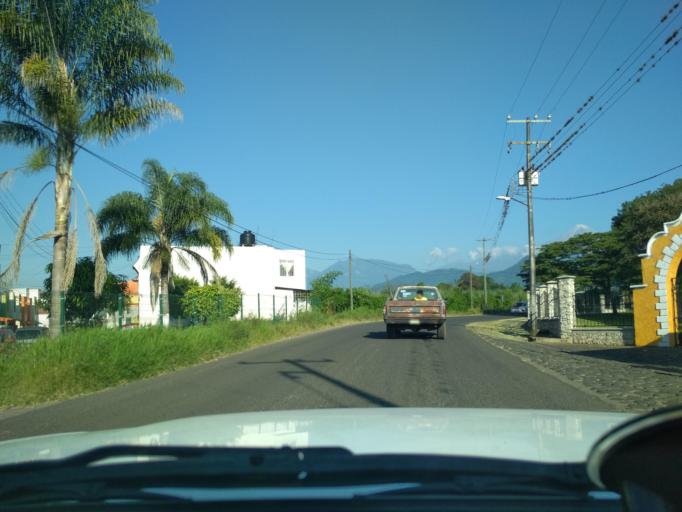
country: MX
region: Veracruz
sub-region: Fortin
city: Fraccionamiento Villas de la Llave
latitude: 18.9212
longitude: -96.9937
